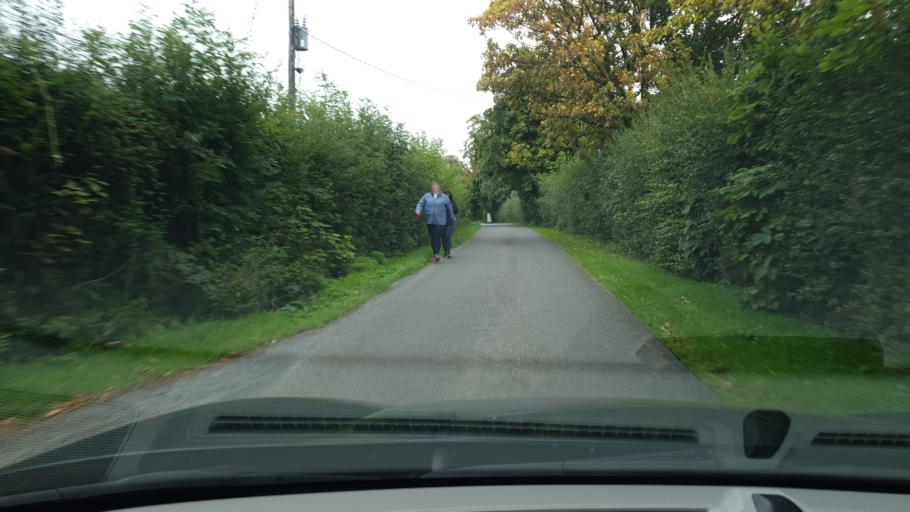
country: IE
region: Leinster
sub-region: An Mhi
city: Dunshaughlin
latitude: 53.4931
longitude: -6.5465
